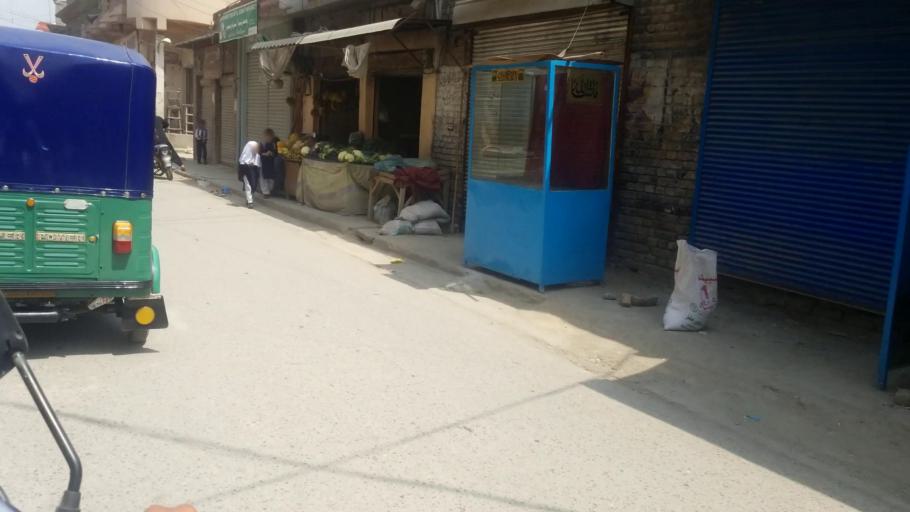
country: PK
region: Khyber Pakhtunkhwa
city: Peshawar
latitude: 34.0302
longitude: 71.5892
